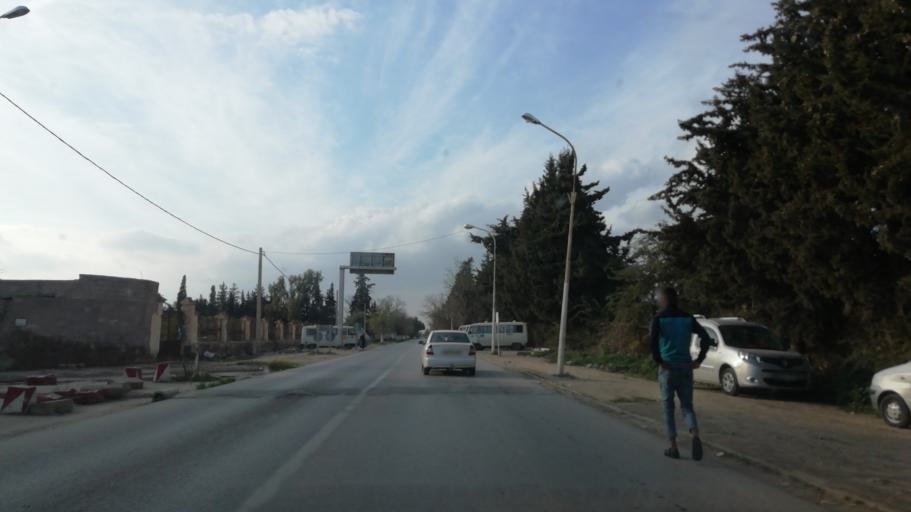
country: DZ
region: Mascara
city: Mascara
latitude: 35.5950
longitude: 0.0627
